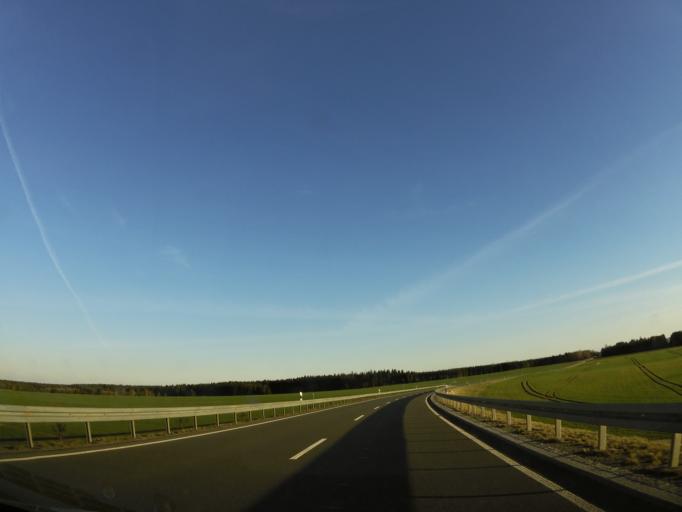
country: DE
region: Thuringia
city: Dittersdorf
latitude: 50.6385
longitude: 11.8140
